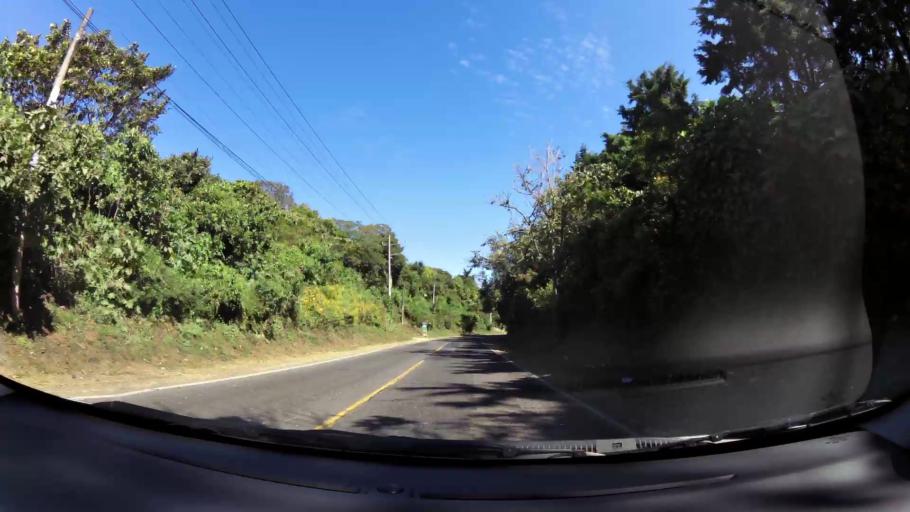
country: SV
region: Ahuachapan
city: Concepcion de Ataco
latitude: 13.8595
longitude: -89.8500
